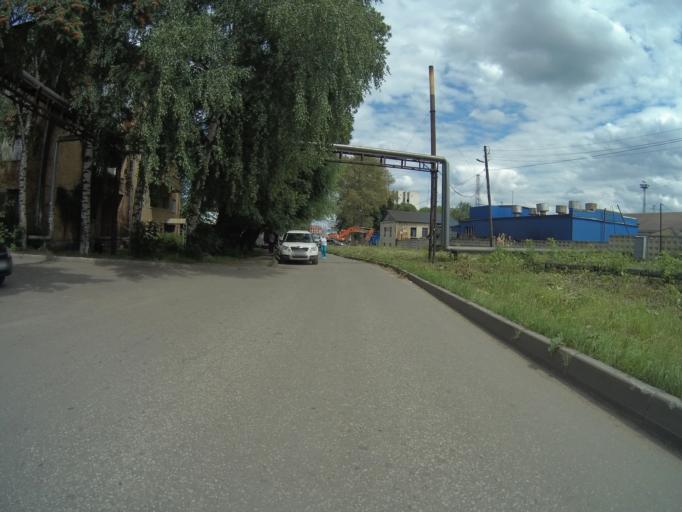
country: RU
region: Vladimir
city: Vladimir
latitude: 56.1291
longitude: 40.4165
